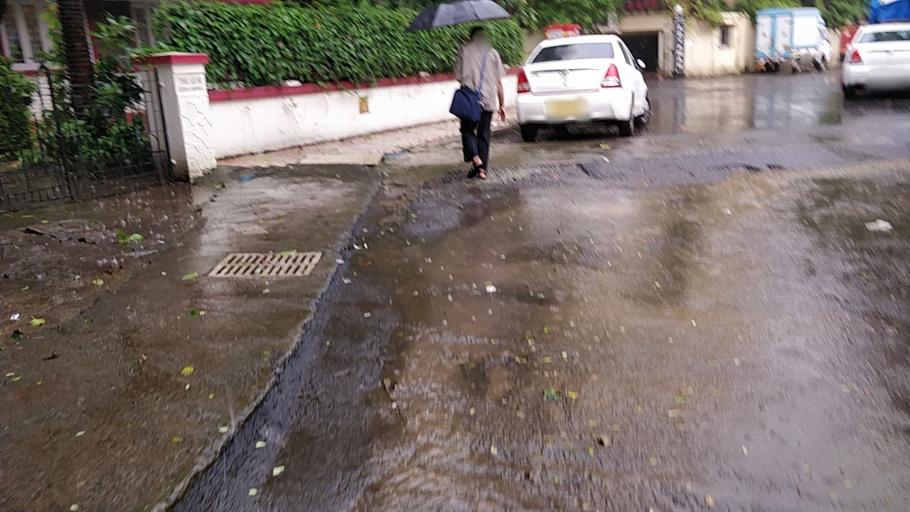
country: IN
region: Maharashtra
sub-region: Mumbai Suburban
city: Mumbai
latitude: 19.0938
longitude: 72.8404
